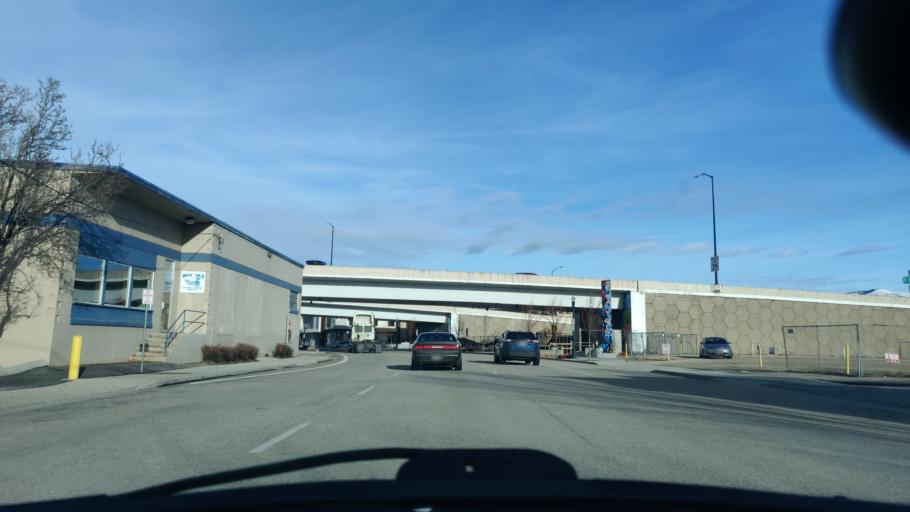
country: US
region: Idaho
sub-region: Ada County
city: Boise
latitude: 43.6176
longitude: -116.2145
